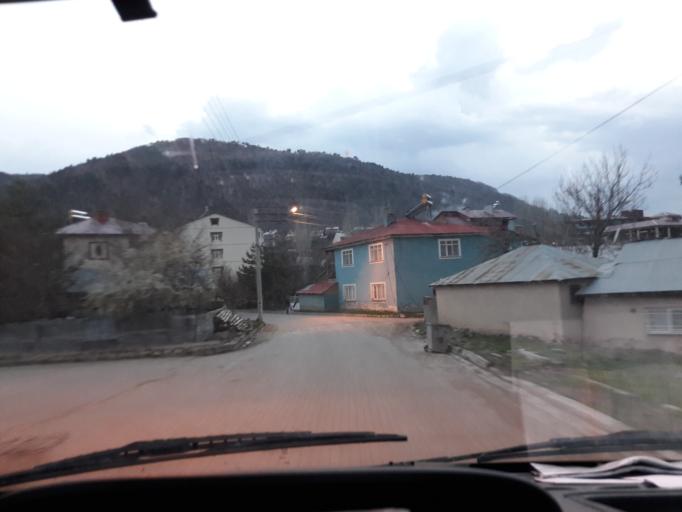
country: TR
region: Giresun
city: Alucra
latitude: 40.3225
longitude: 38.7660
